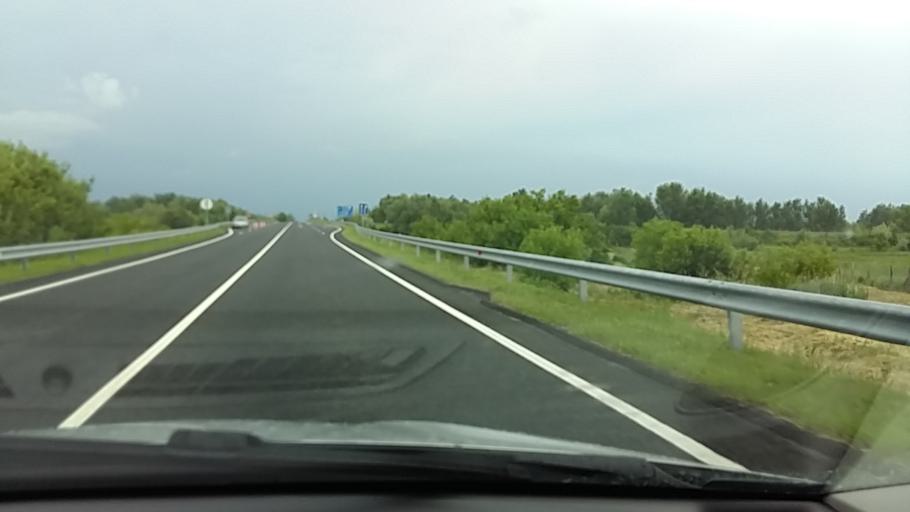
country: HU
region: Somogy
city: Balatonfenyves
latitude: 46.7035
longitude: 17.4697
